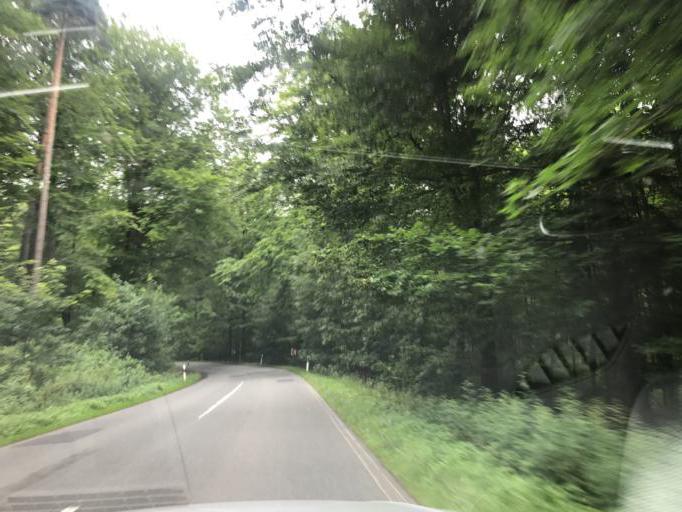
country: DE
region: Mecklenburg-Vorpommern
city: Rechlin
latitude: 53.2360
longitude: 12.7027
